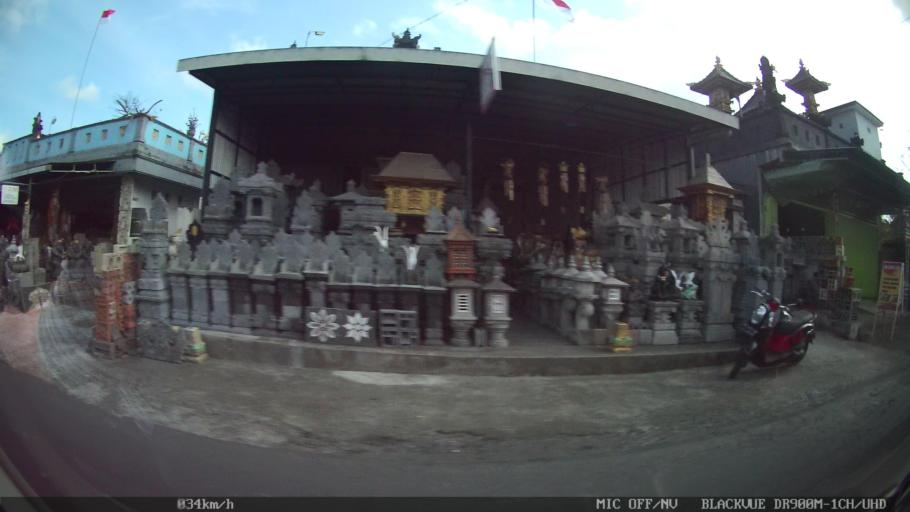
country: ID
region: Bali
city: Banjar Pekenjelodan
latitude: -8.5717
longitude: 115.1882
